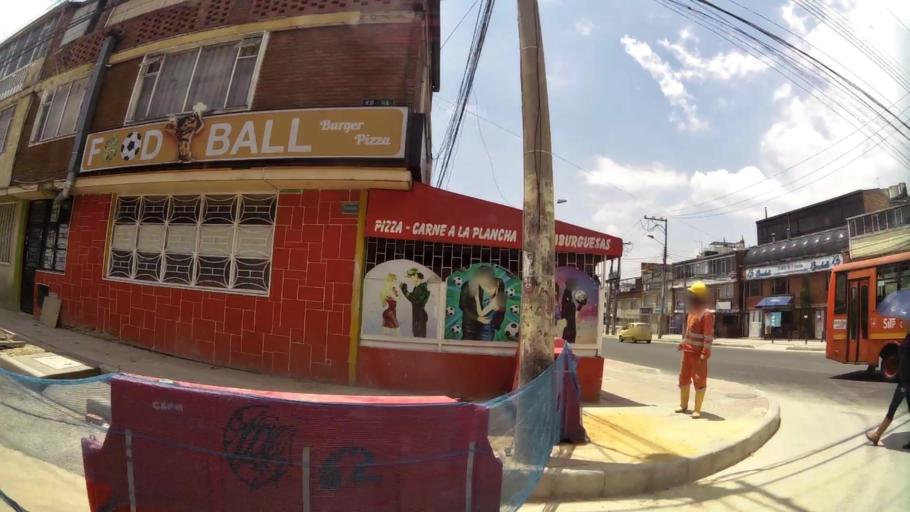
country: CO
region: Bogota D.C.
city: Bogota
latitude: 4.5778
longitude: -74.0922
